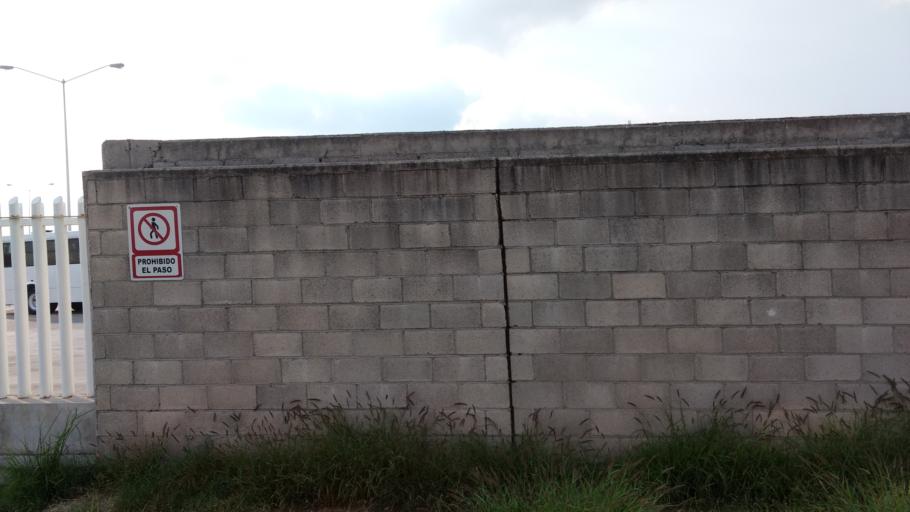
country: MX
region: Guanajuato
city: Leon
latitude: 21.1500
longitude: -101.6761
